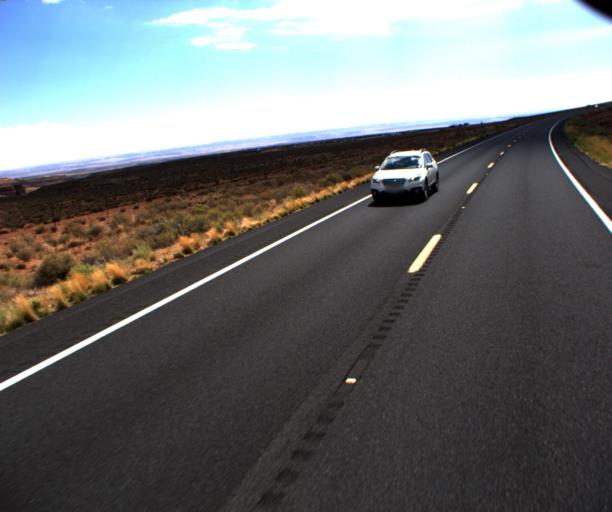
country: US
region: Arizona
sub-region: Coconino County
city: Tuba City
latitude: 35.9199
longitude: -111.5717
